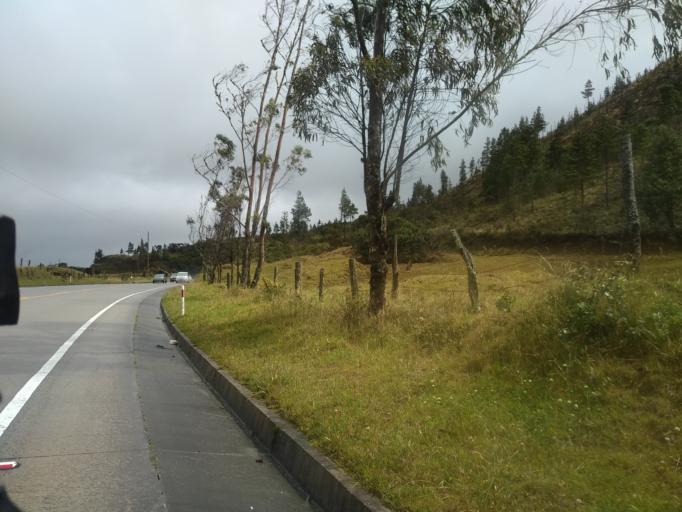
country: EC
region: Loja
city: Loja
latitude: -3.8905
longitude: -79.2622
